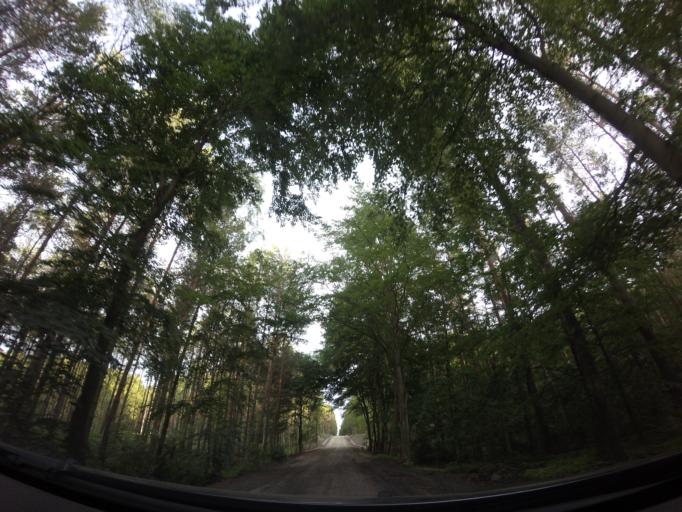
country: PL
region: West Pomeranian Voivodeship
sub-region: Powiat choszczenski
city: Bierzwnik
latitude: 53.0235
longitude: 15.6040
